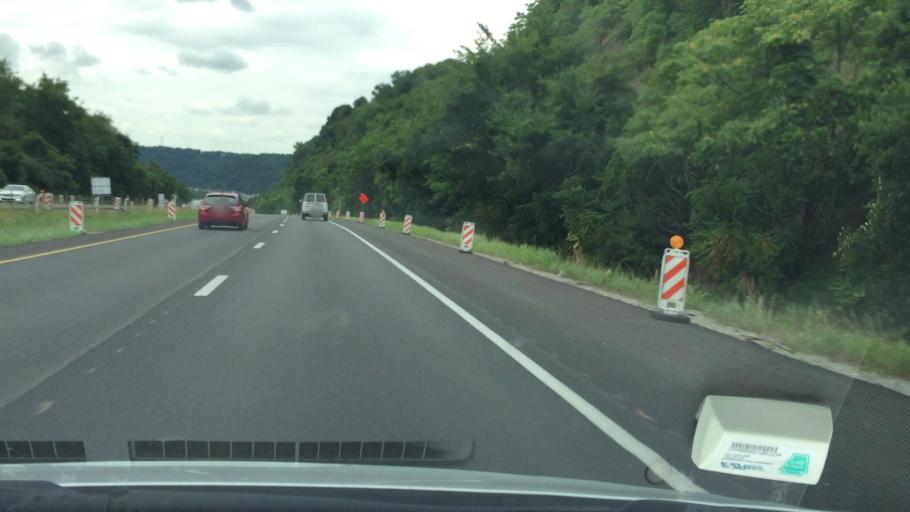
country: US
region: Pennsylvania
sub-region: Allegheny County
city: Tarentum
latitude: 40.6022
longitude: -79.7674
